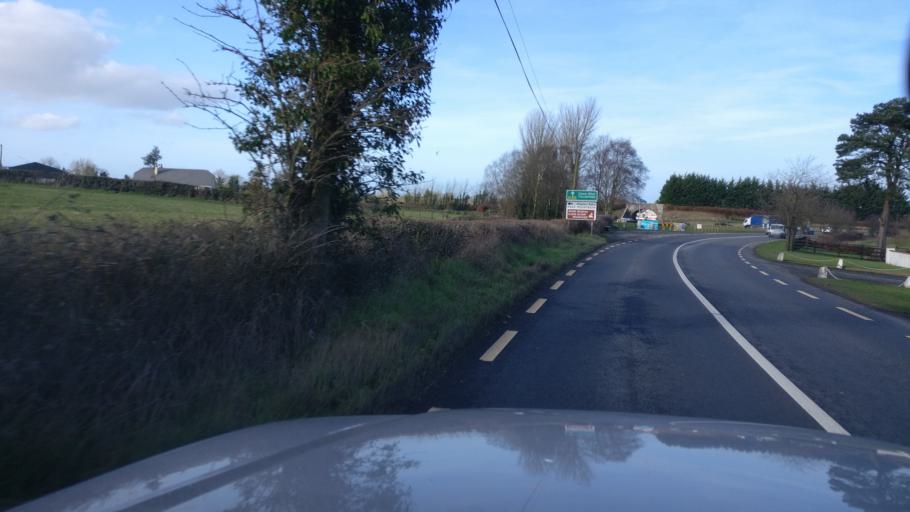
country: IE
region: Leinster
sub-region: Laois
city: Mountmellick
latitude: 53.0998
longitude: -7.3387
